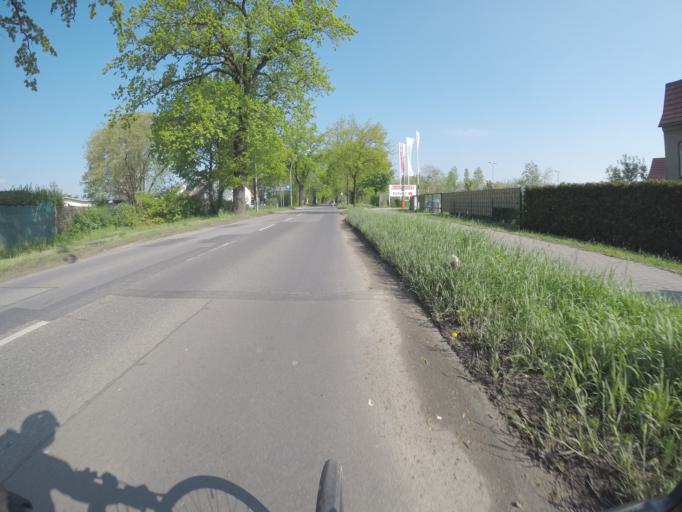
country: DE
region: Berlin
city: Buchholz
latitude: 52.6149
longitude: 13.4319
